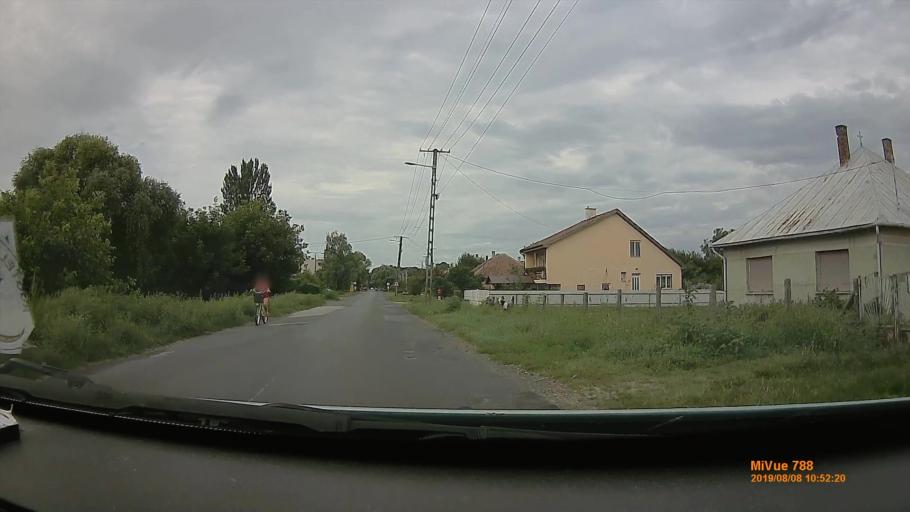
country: HU
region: Szabolcs-Szatmar-Bereg
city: Balkany
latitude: 47.7701
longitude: 21.8443
